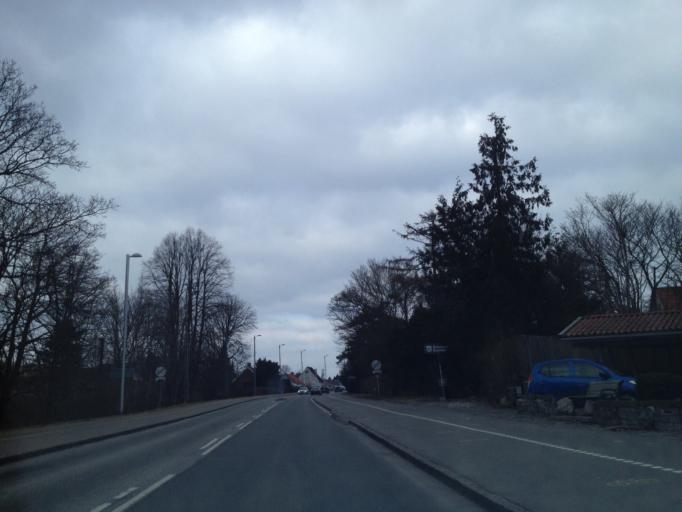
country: DK
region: Capital Region
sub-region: Fredensborg Kommune
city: Humlebaek
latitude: 55.9788
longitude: 12.5447
